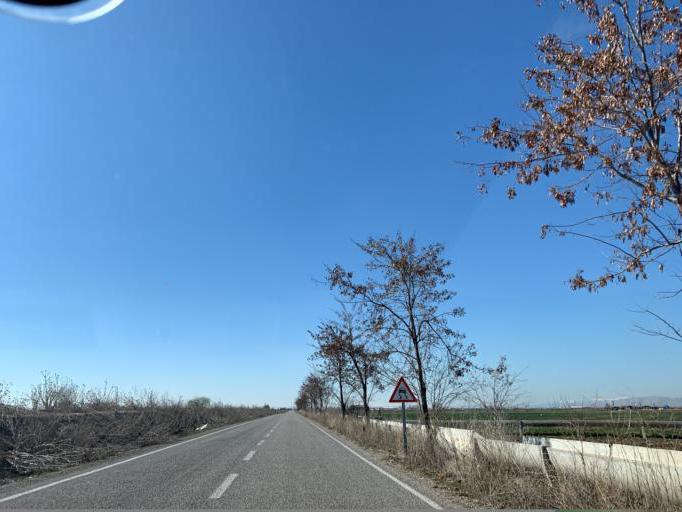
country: TR
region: Konya
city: Catalhoeyuek
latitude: 37.6216
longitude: 32.8025
